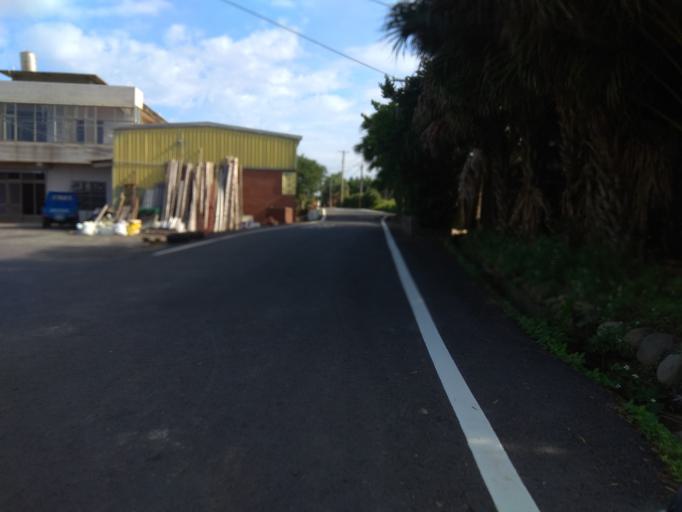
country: TW
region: Taiwan
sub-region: Hsinchu
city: Zhubei
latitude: 25.0010
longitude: 121.0450
